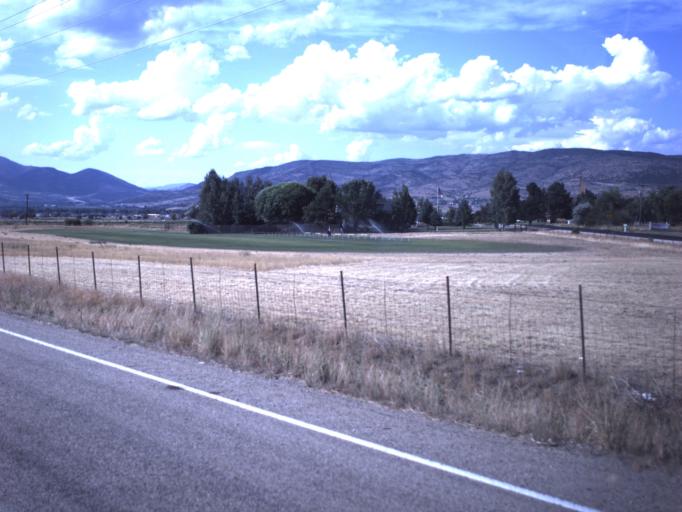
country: US
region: Utah
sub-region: Wasatch County
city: Heber
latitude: 40.4759
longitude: -111.3959
